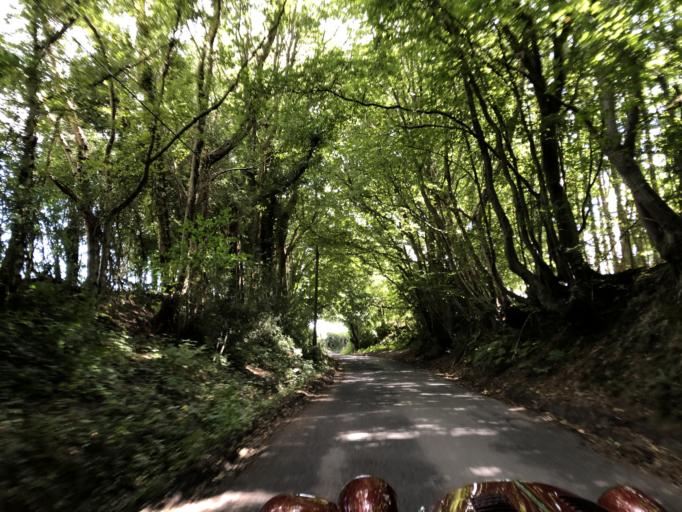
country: GB
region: England
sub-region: East Sussex
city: Northiam
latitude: 50.9863
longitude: 0.5822
